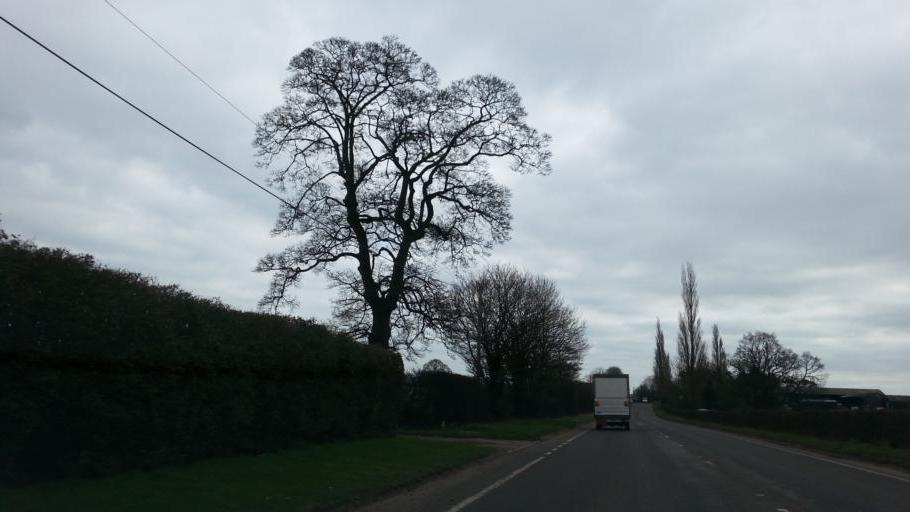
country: GB
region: England
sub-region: Staffordshire
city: Stone
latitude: 52.8748
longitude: -2.1004
